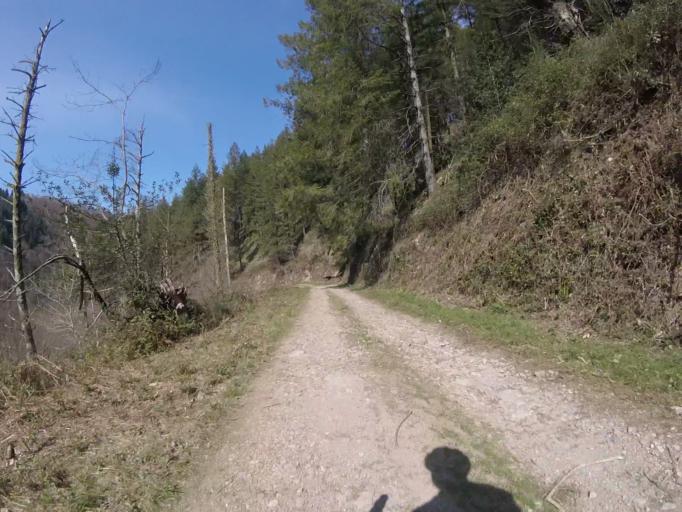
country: ES
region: Basque Country
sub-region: Provincia de Guipuzcoa
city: Irun
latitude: 43.2551
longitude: -1.8056
